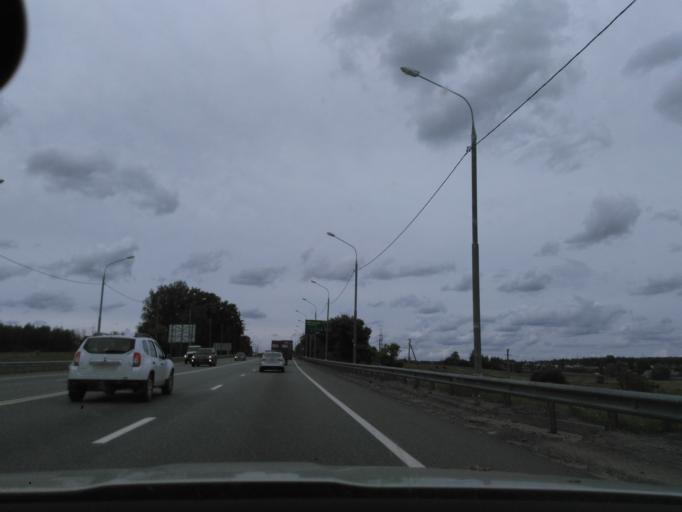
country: RU
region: Moskovskaya
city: Klin
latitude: 56.3022
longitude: 36.7922
